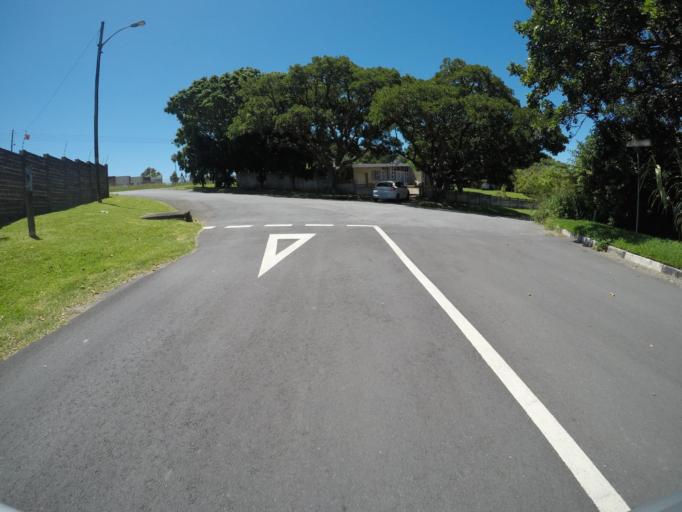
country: ZA
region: Eastern Cape
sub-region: Buffalo City Metropolitan Municipality
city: East London
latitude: -32.9586
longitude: 27.9408
